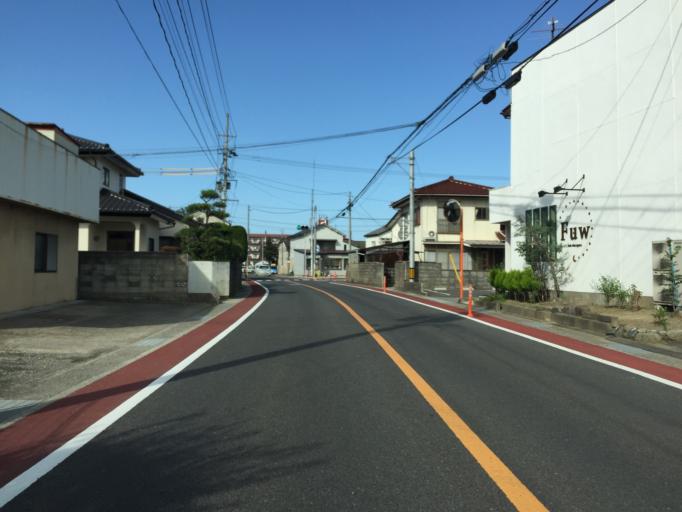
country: JP
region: Fukushima
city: Fukushima-shi
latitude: 37.7740
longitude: 140.4972
